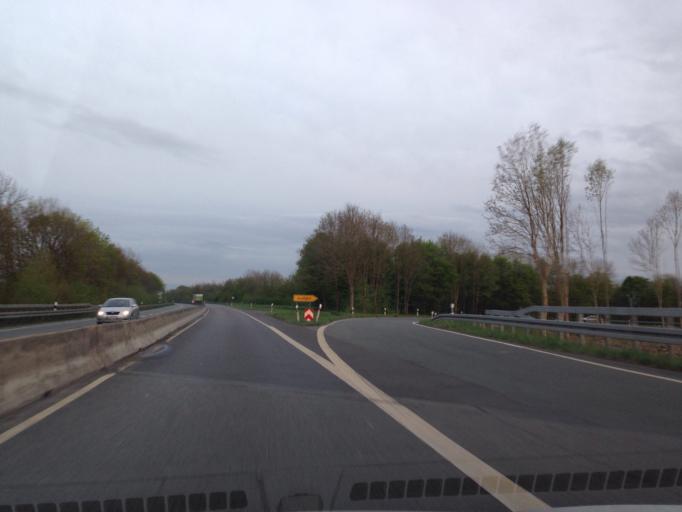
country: DE
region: North Rhine-Westphalia
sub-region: Regierungsbezirk Munster
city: Altenberge
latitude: 52.0444
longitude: 7.4489
